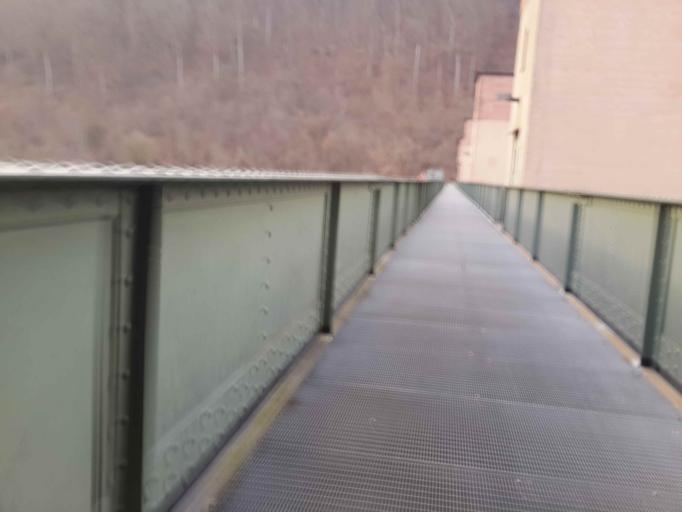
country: DE
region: Baden-Wuerttemberg
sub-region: Karlsruhe Region
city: Neckargerach
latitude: 49.3833
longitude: 9.0769
